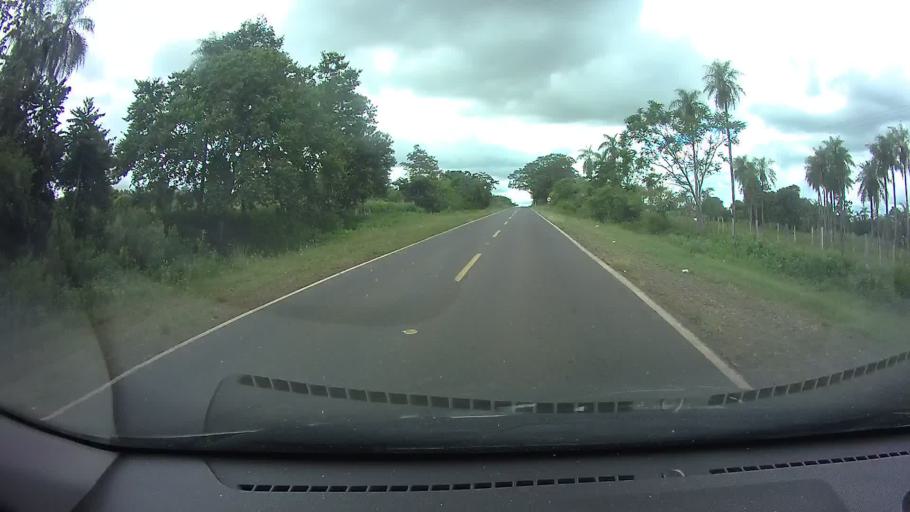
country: PY
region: Paraguari
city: Acahay
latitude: -25.9129
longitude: -57.0590
